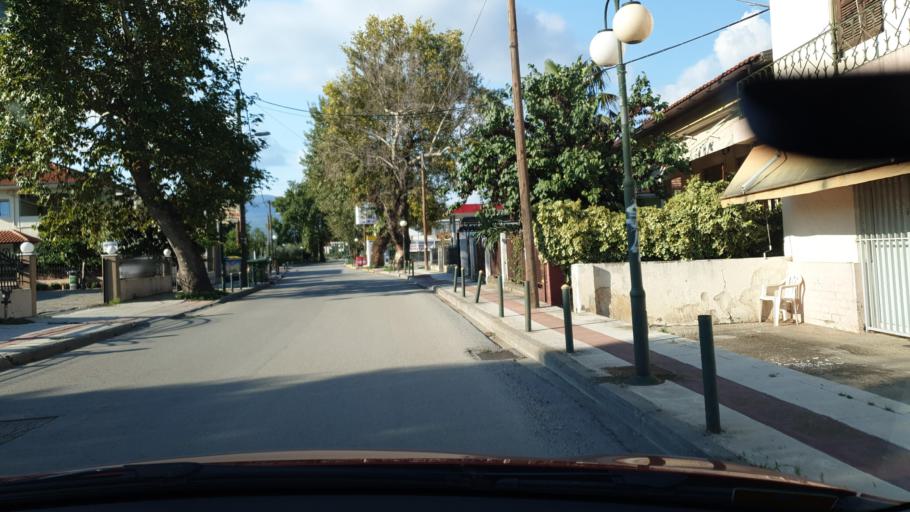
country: GR
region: Central Macedonia
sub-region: Nomos Thessalonikis
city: Vasilika
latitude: 40.4846
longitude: 23.1378
